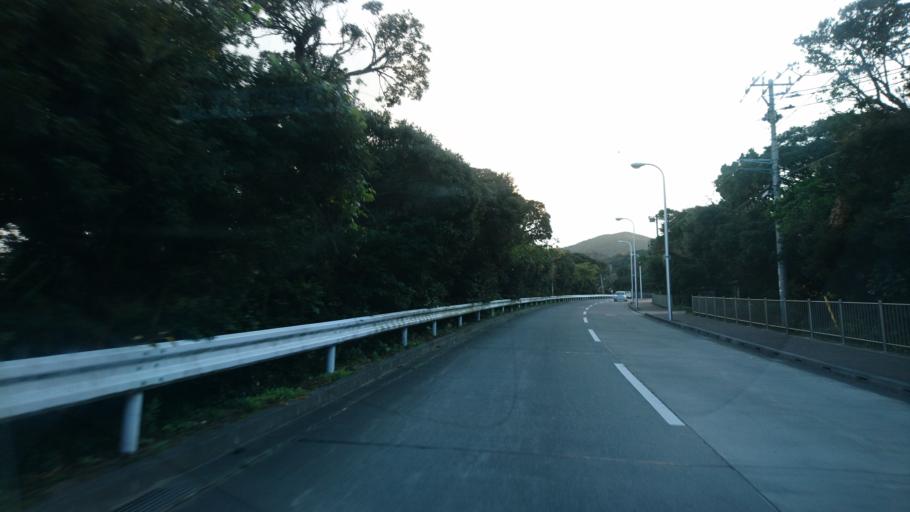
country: JP
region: Shizuoka
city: Shimoda
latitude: 34.3692
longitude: 139.2591
